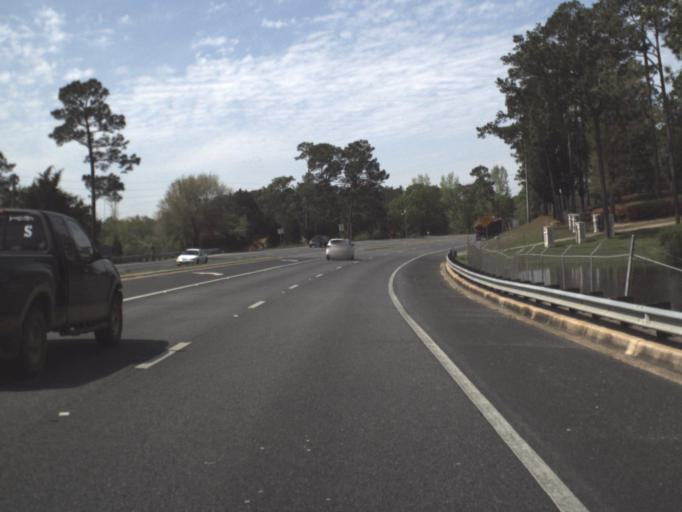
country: US
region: Florida
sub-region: Okaloosa County
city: Crestview
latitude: 30.7544
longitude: -86.6158
